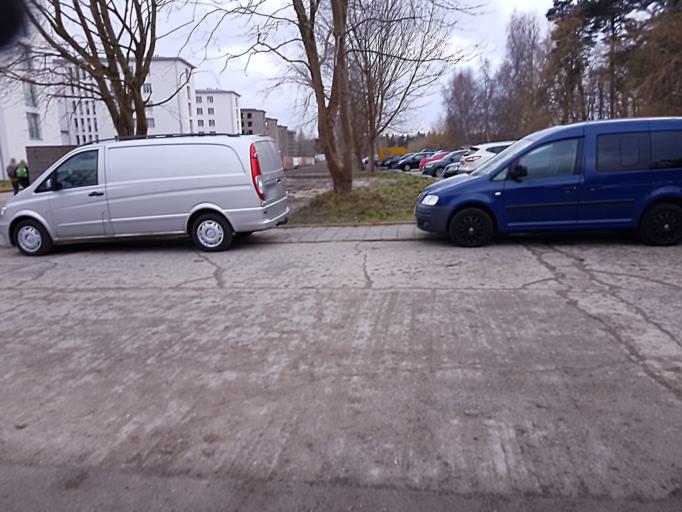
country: DE
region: Mecklenburg-Vorpommern
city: Ostseebad Binz
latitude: 54.4459
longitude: 13.5711
